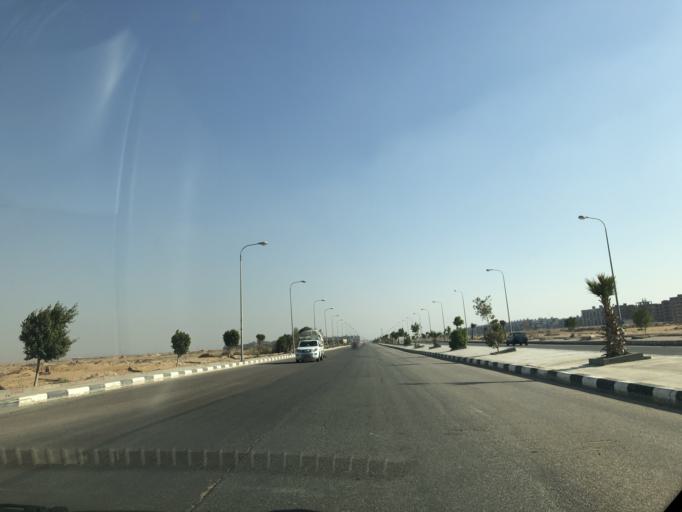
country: EG
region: Al Jizah
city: Madinat Sittah Uktubar
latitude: 29.9167
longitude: 31.0643
